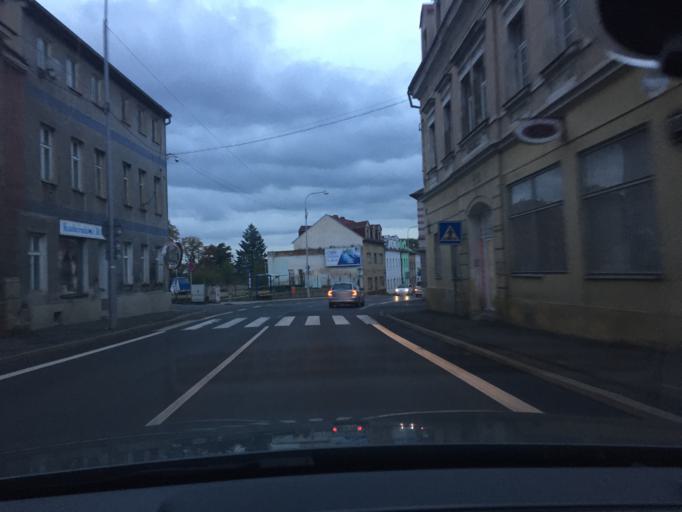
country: CZ
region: Ustecky
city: Dubi
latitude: 50.6634
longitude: 13.7981
